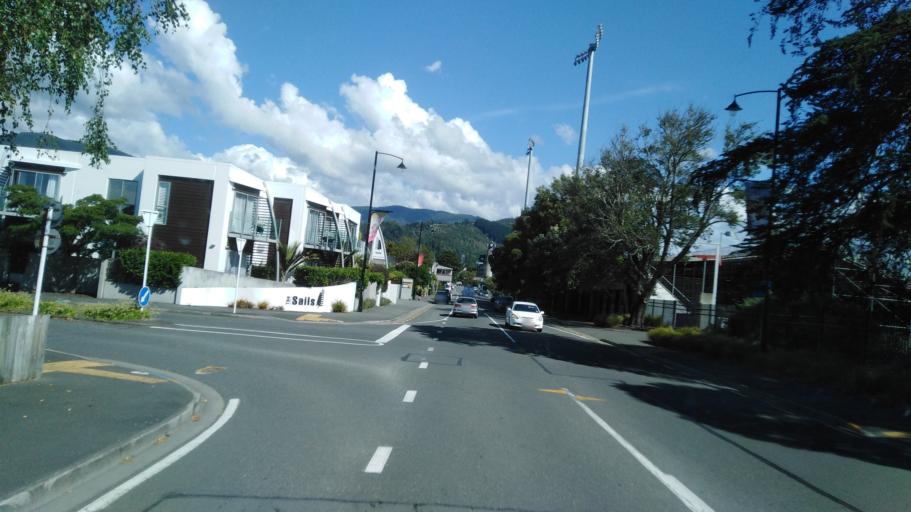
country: NZ
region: Nelson
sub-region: Nelson City
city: Nelson
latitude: -41.2660
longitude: 173.2842
